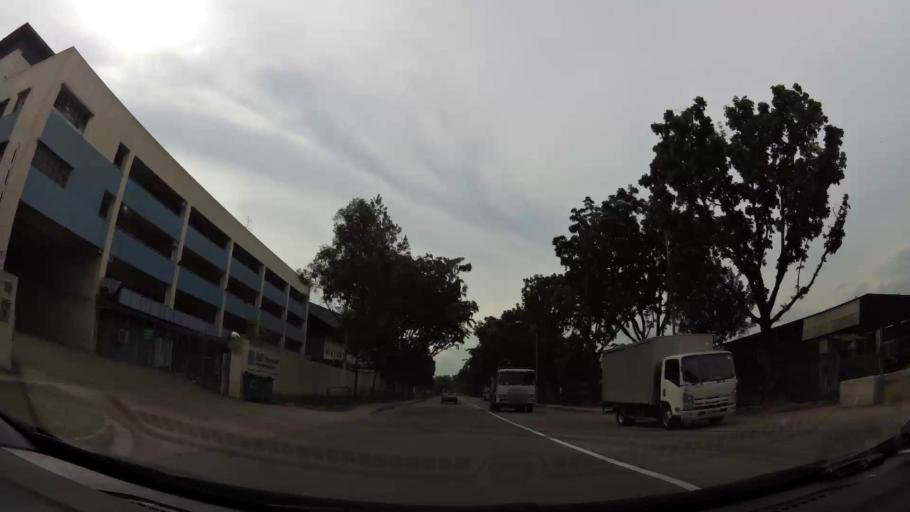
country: MY
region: Johor
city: Johor Bahru
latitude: 1.4362
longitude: 103.7476
